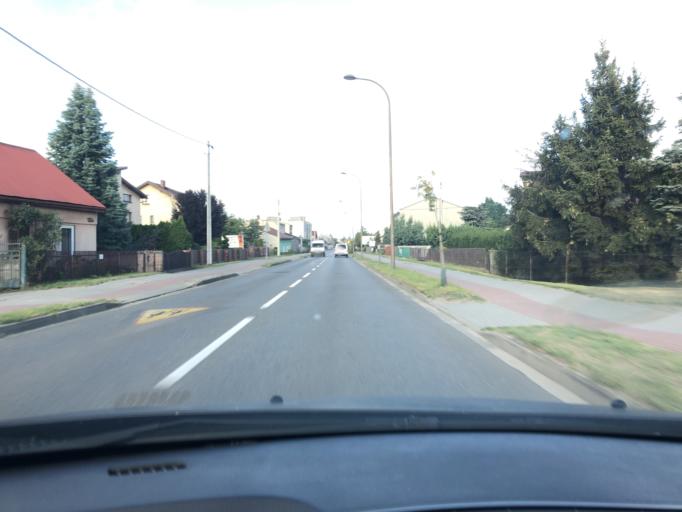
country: PL
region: Lodz Voivodeship
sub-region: Powiat wieruszowski
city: Wieruszow
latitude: 51.2951
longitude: 18.1681
